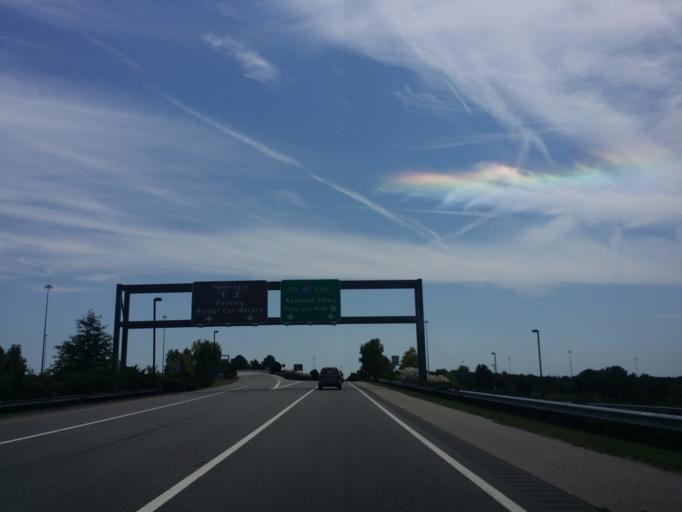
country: US
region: North Carolina
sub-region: Wake County
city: Morrisville
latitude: 35.8693
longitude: -78.8057
